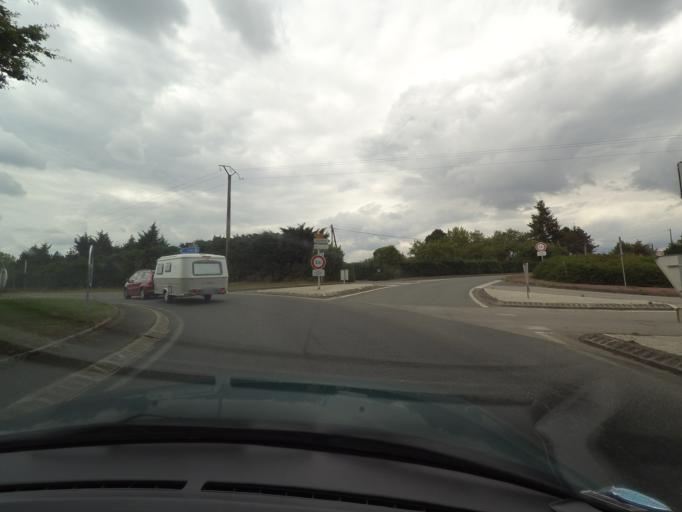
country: FR
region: Poitou-Charentes
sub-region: Departement des Deux-Sevres
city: Chatillon-sur-Thouet
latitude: 46.6653
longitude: -0.2365
